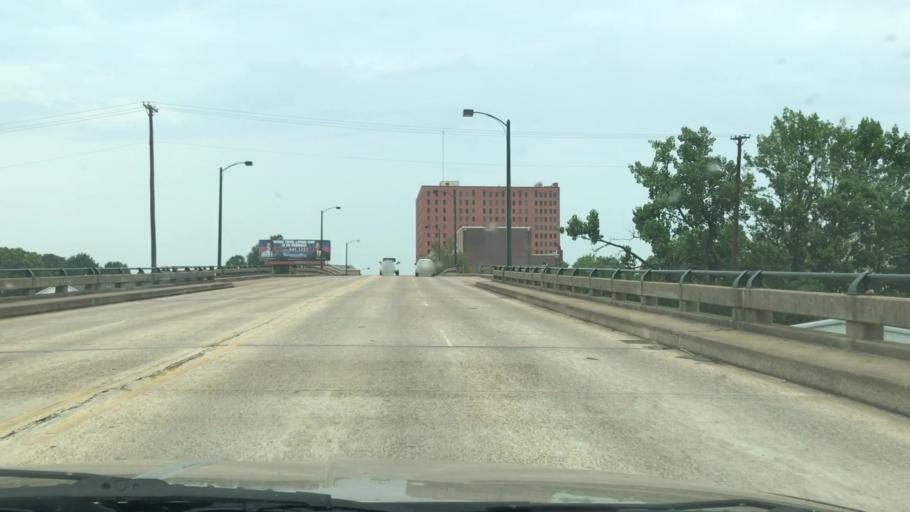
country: US
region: Louisiana
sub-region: Bossier Parish
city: Bossier City
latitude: 32.5063
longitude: -93.7482
